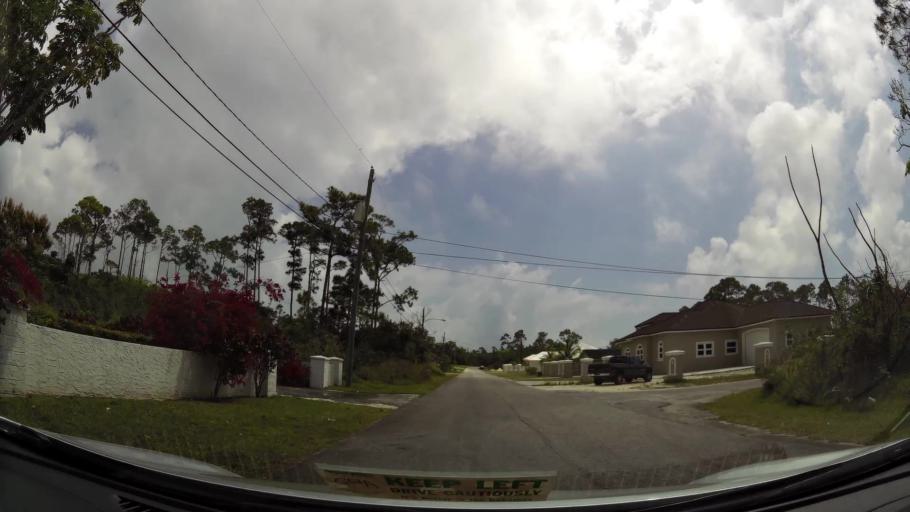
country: BS
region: Freeport
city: Lucaya
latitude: 26.5234
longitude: -78.6511
